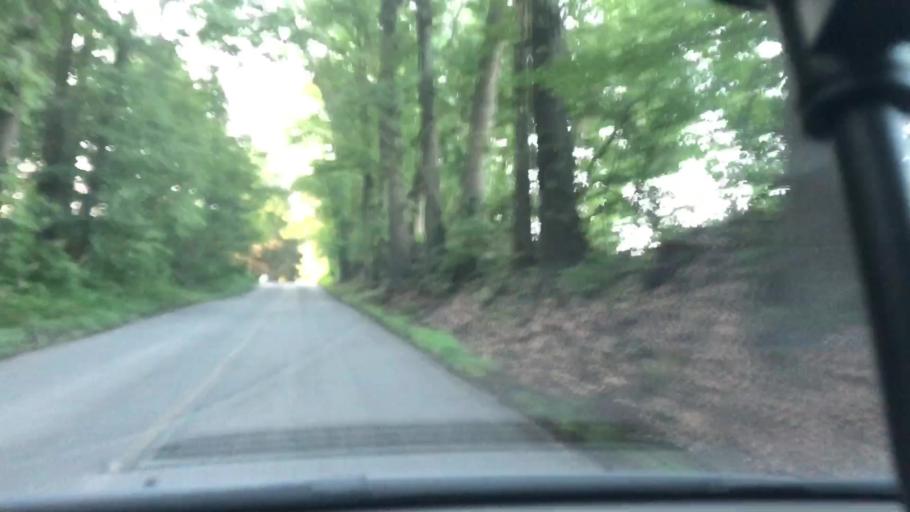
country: US
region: Pennsylvania
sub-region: Chester County
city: Kenilworth
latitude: 40.1878
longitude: -75.6448
